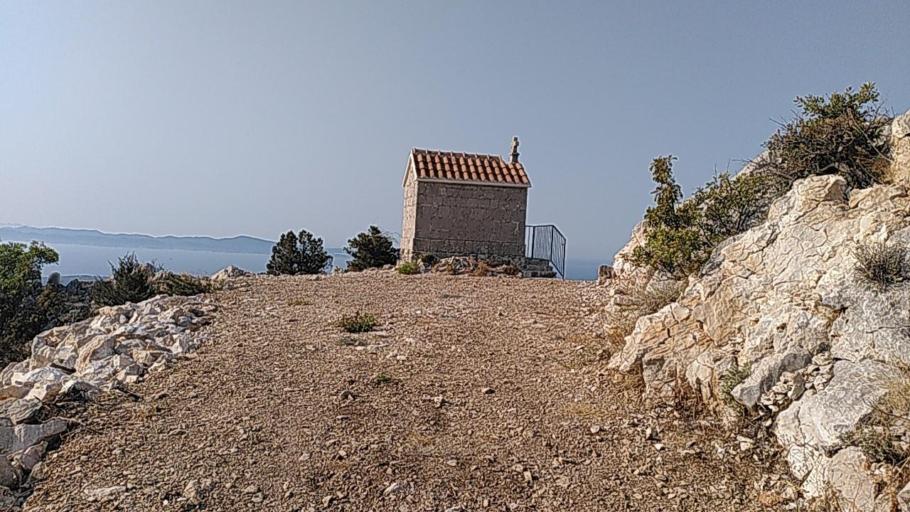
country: HR
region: Splitsko-Dalmatinska
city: Jelsa
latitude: 43.1330
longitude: 16.6805
